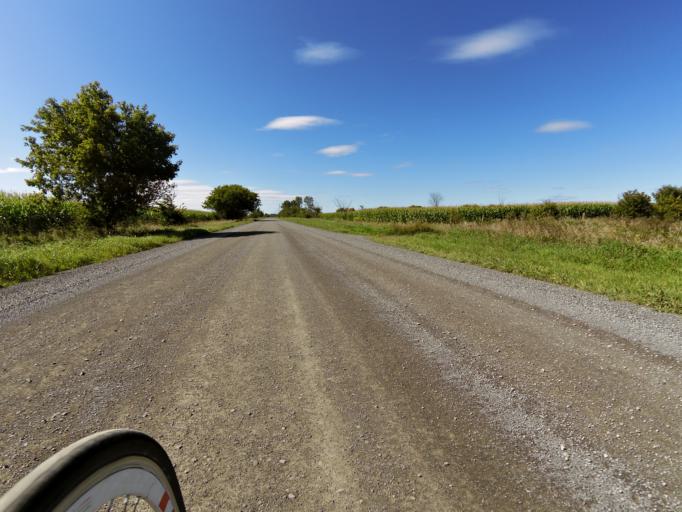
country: CA
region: Ontario
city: Bells Corners
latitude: 45.2269
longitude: -75.8374
